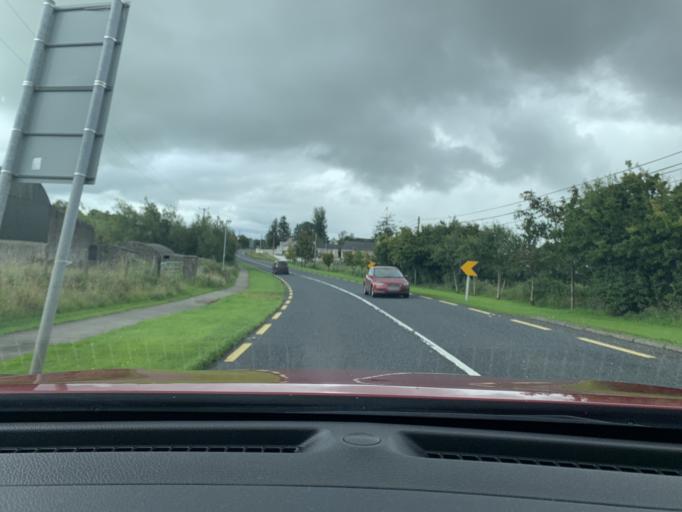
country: IE
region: Ulster
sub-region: County Donegal
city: Raphoe
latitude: 54.8008
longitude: -7.5811
